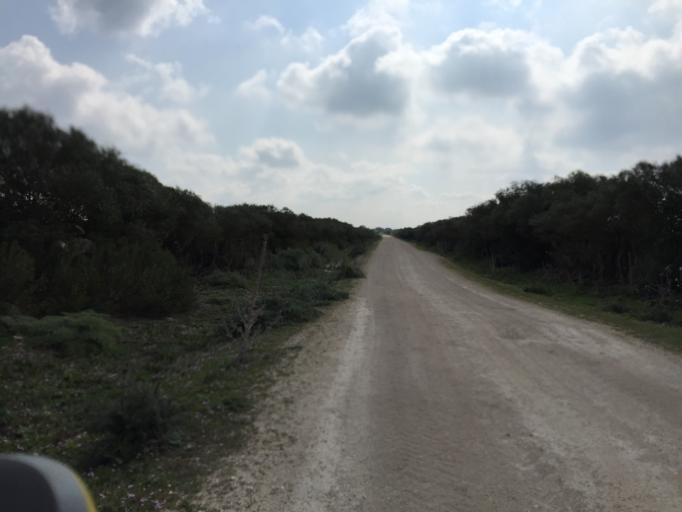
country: ES
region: Andalusia
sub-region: Provincia de Cadiz
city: Benalup-Casas Viejas
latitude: 36.3288
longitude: -5.8905
